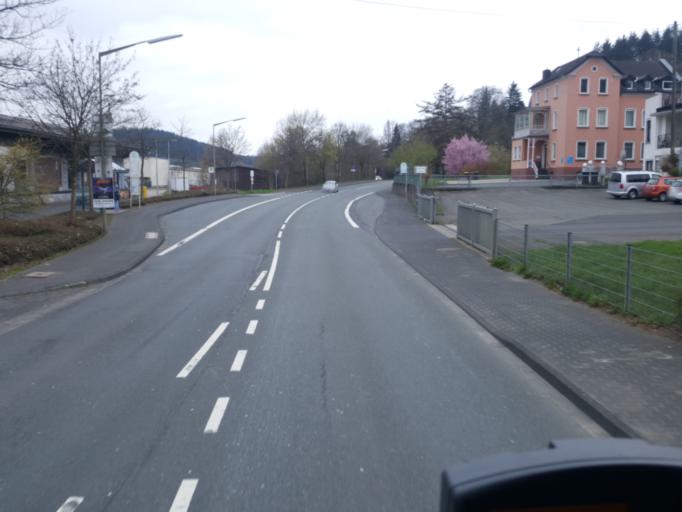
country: DE
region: North Rhine-Westphalia
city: Hilchenbach
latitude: 50.9928
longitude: 8.1069
